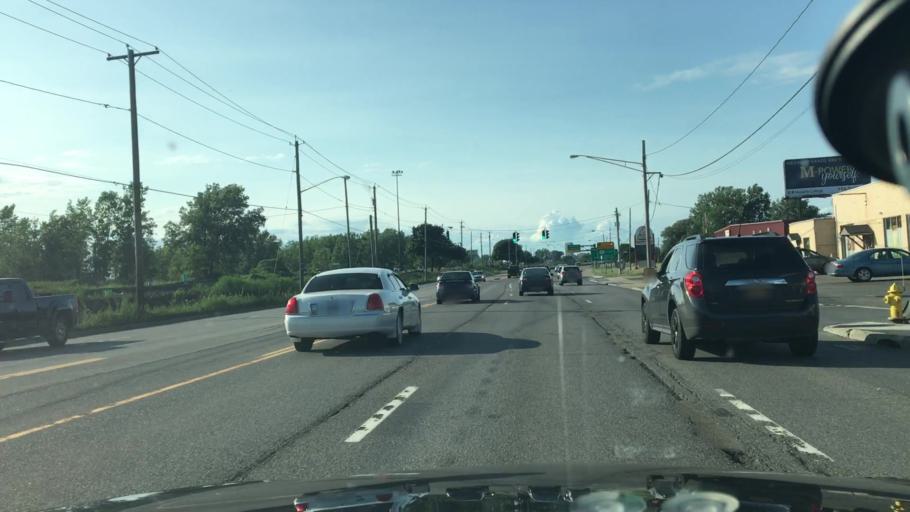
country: US
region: New York
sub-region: Erie County
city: Lackawanna
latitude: 42.8201
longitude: -78.8480
